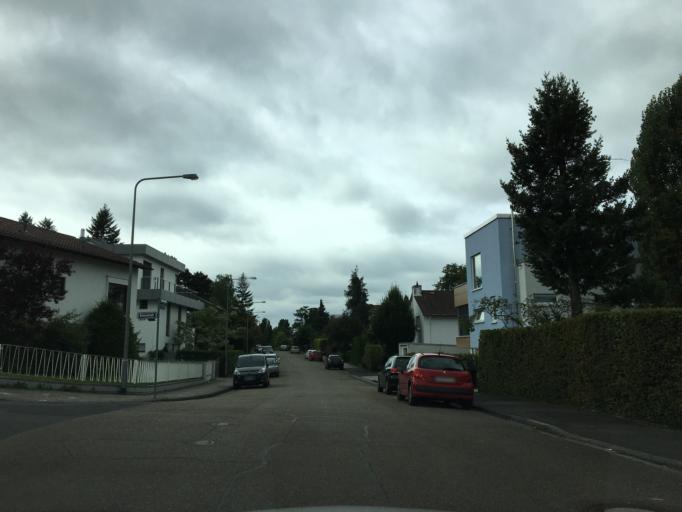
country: DE
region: Hesse
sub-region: Regierungsbezirk Darmstadt
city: Wiesbaden
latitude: 50.0858
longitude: 8.2651
